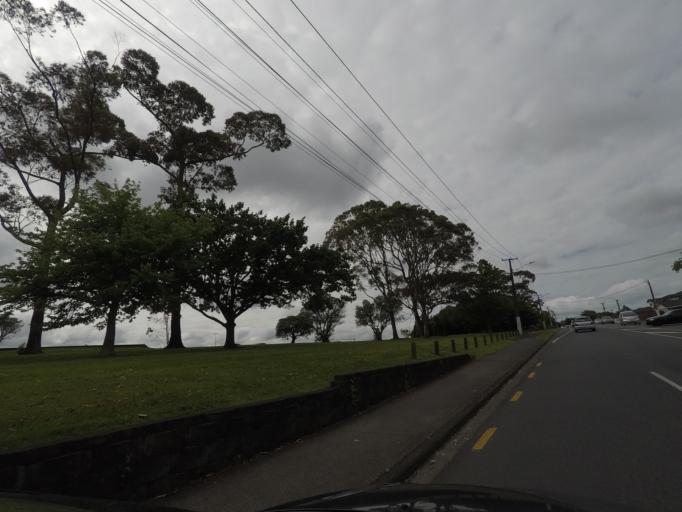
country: NZ
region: Auckland
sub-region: Auckland
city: Waitakere
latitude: -36.9055
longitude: 174.6268
